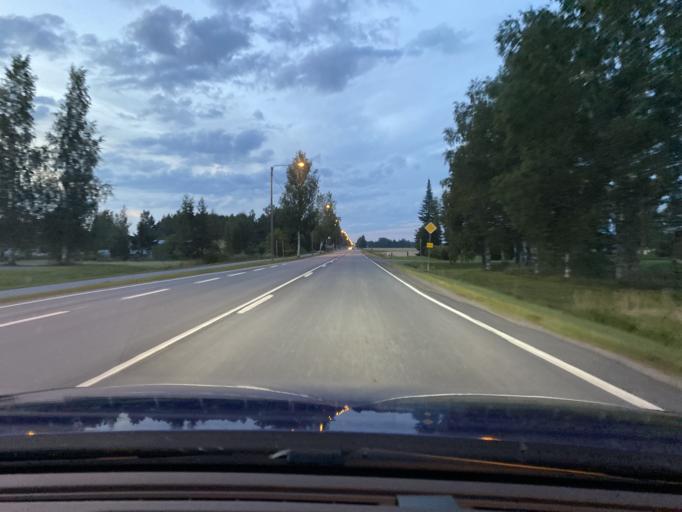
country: FI
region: Southern Ostrobothnia
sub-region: Suupohja
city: Kauhajoki
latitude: 62.4307
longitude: 22.2042
